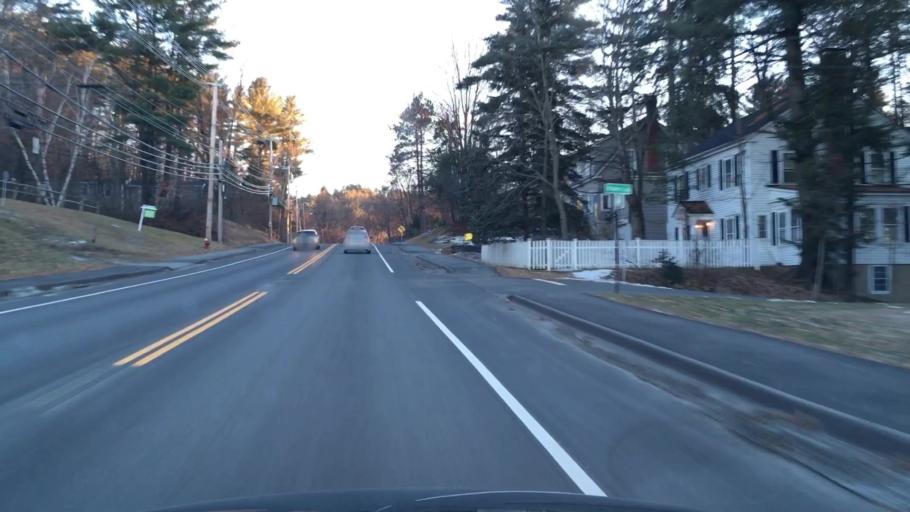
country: US
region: New Hampshire
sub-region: Grafton County
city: Hanover
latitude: 43.6953
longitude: -72.2796
